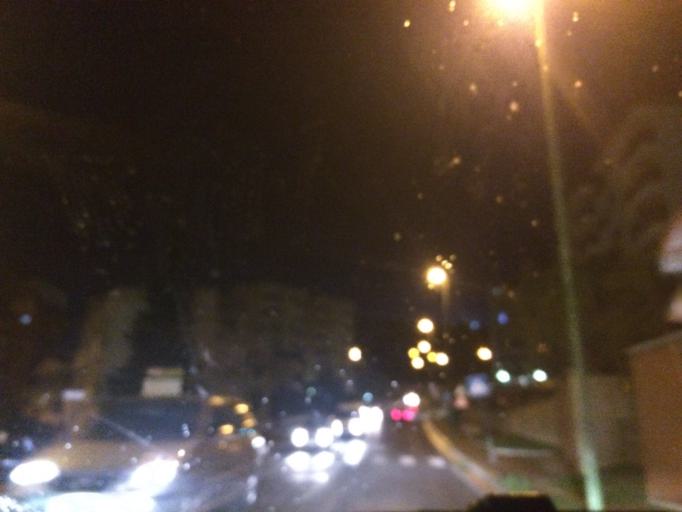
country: IT
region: Basilicate
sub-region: Provincia di Matera
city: Matera
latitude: 40.6707
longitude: 16.5934
